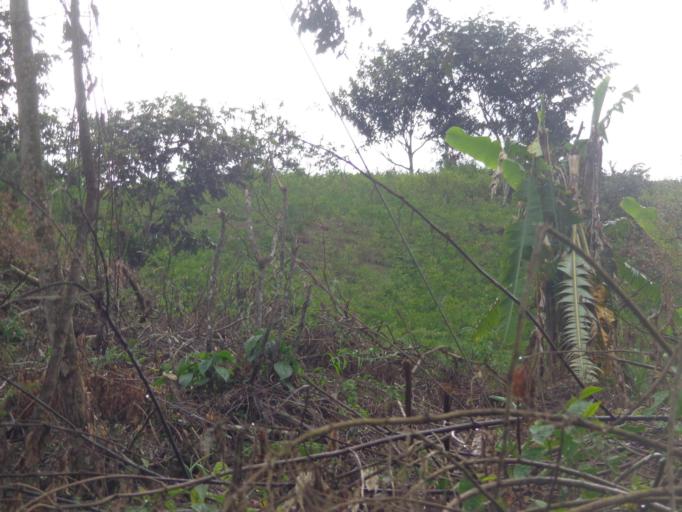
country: BO
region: La Paz
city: Coroico
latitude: -16.1314
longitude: -67.7516
